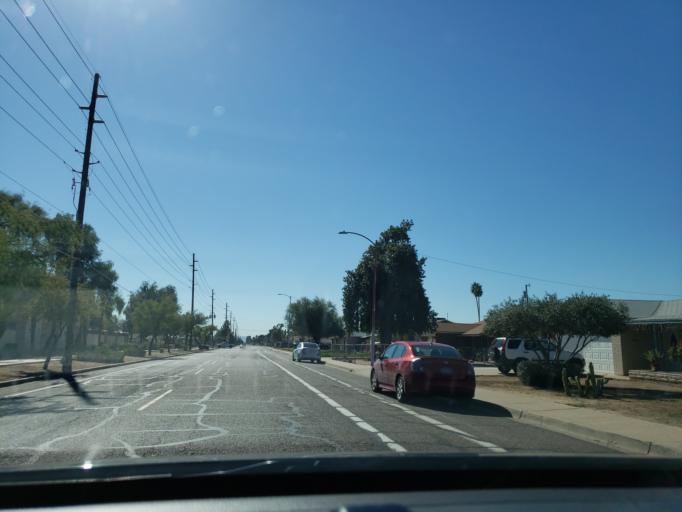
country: US
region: Arizona
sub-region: Maricopa County
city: Glendale
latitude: 33.6052
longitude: -112.1253
